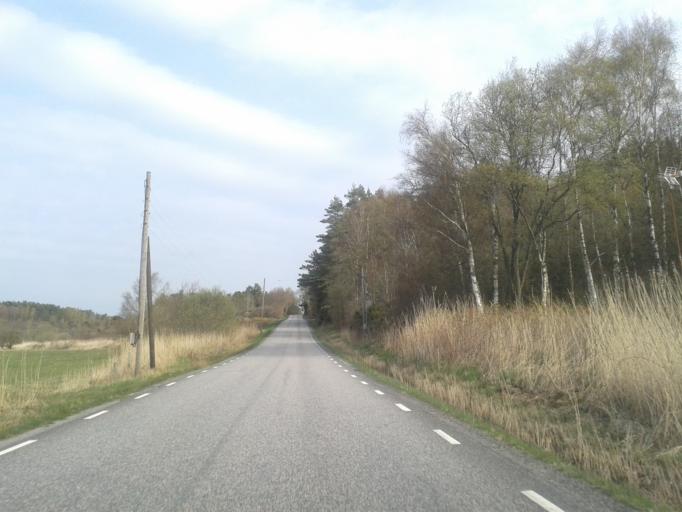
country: SE
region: Vaestra Goetaland
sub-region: Kungalvs Kommun
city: Kode
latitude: 57.9022
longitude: 11.8053
